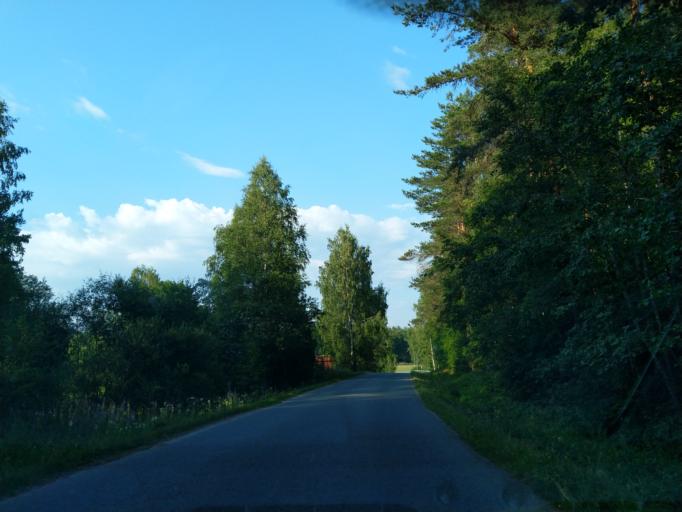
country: FI
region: Satakunta
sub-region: Pohjois-Satakunta
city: Honkajoki
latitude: 61.8147
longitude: 22.1945
